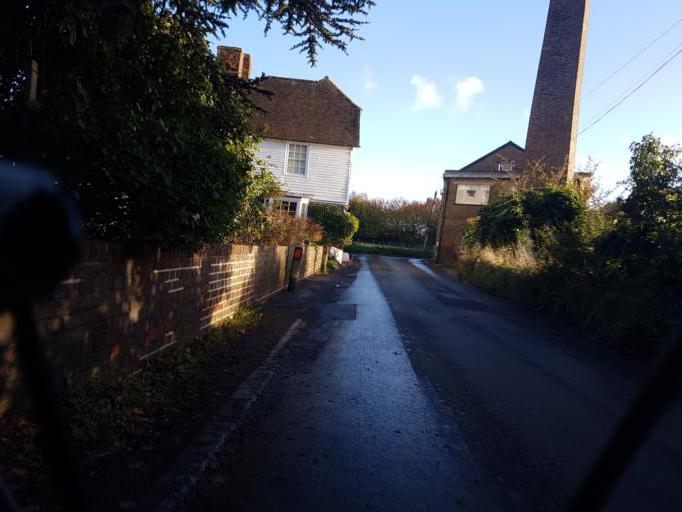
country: GB
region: England
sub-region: Kent
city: Teynham
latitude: 51.3387
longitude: 0.7755
